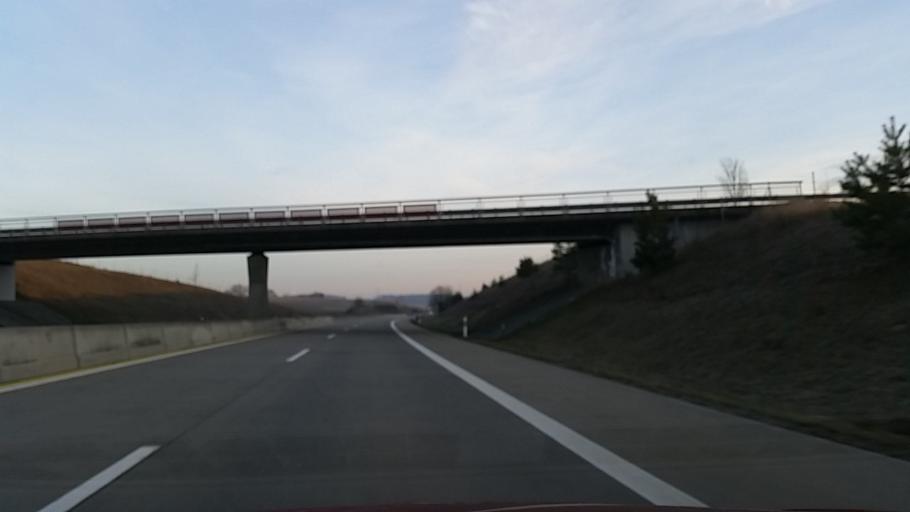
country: DE
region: Bavaria
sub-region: Regierungsbezirk Unterfranken
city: Rodelmaier
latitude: 50.3072
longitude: 10.2808
